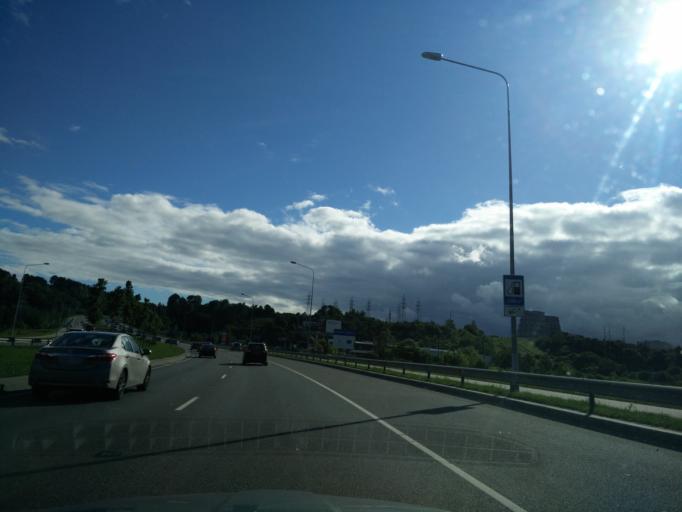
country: LT
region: Vilnius County
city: Lazdynai
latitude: 54.6688
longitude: 25.1771
